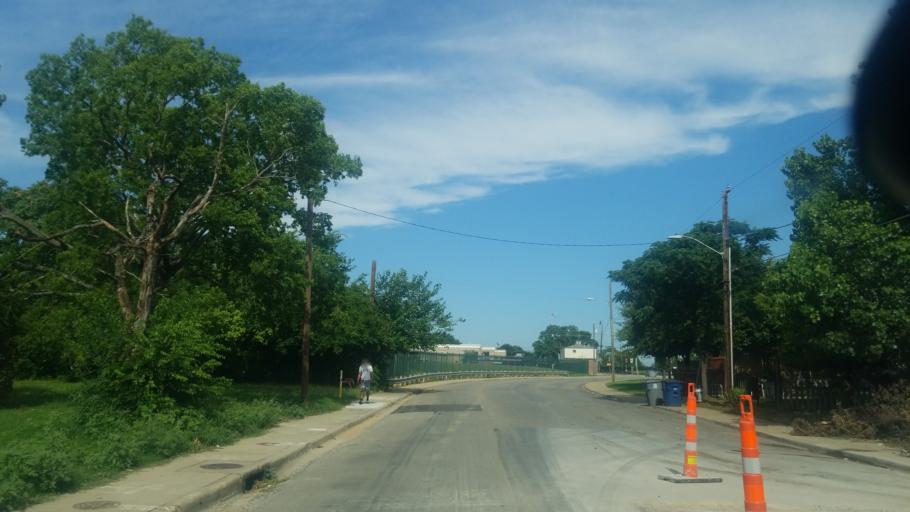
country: US
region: Texas
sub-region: Dallas County
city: Dallas
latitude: 32.7818
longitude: -96.8545
